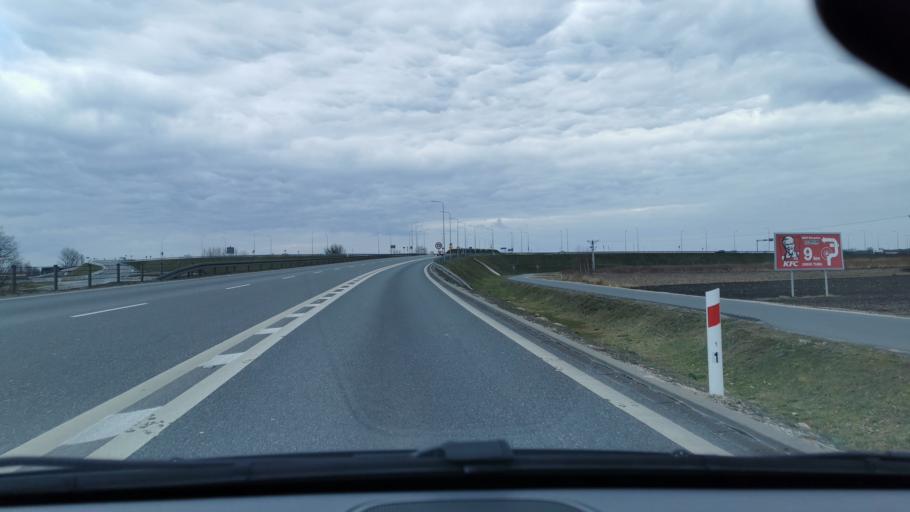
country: PL
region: Masovian Voivodeship
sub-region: Powiat zyrardowski
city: Wiskitki
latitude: 52.0938
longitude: 20.3630
